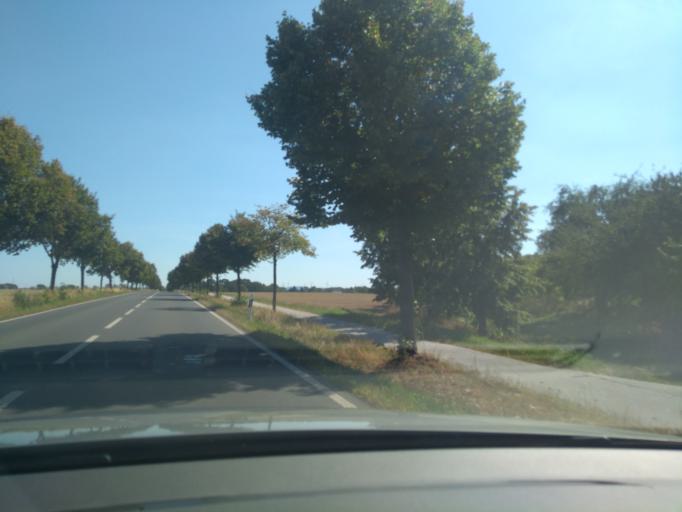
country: DE
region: Saxony
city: Panschwitz-Kuckau
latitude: 51.2324
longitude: 14.2053
